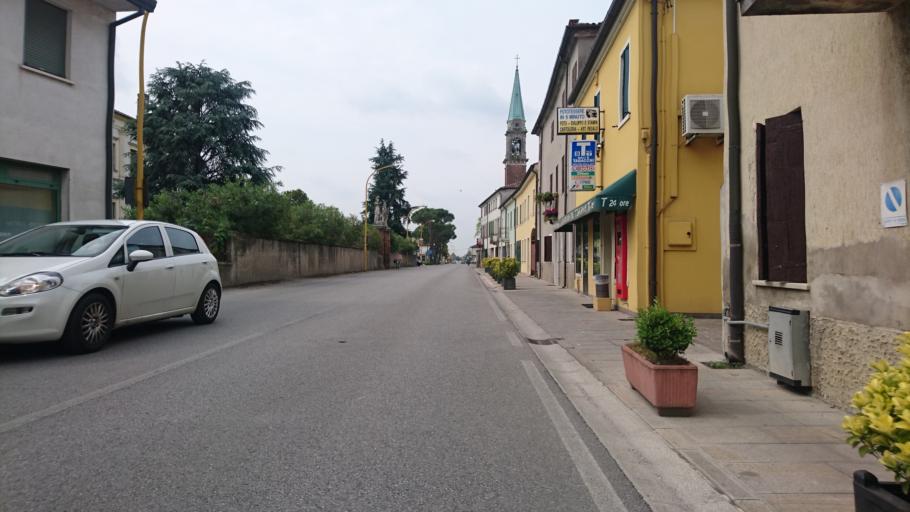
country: IT
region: Veneto
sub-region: Provincia di Padova
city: Villa Estense
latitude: 45.1733
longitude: 11.6682
